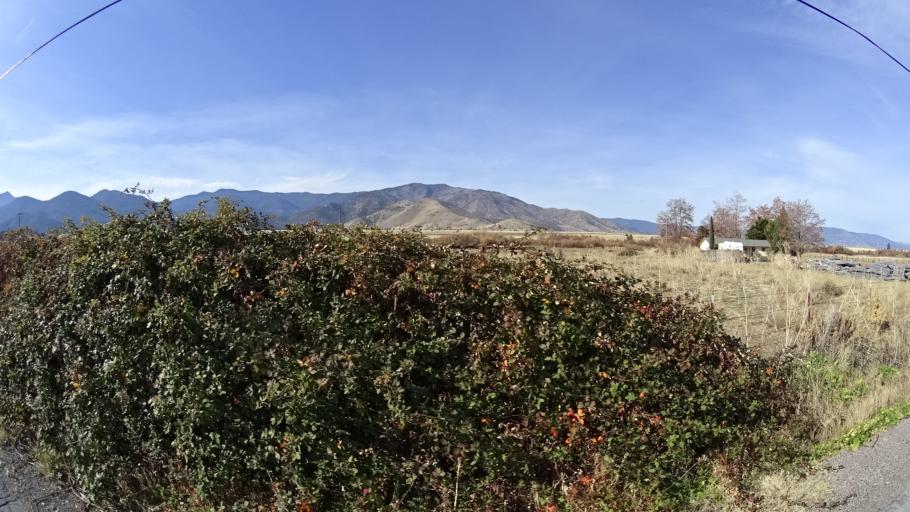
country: US
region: California
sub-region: Siskiyou County
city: Weed
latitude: 41.4642
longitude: -122.4341
